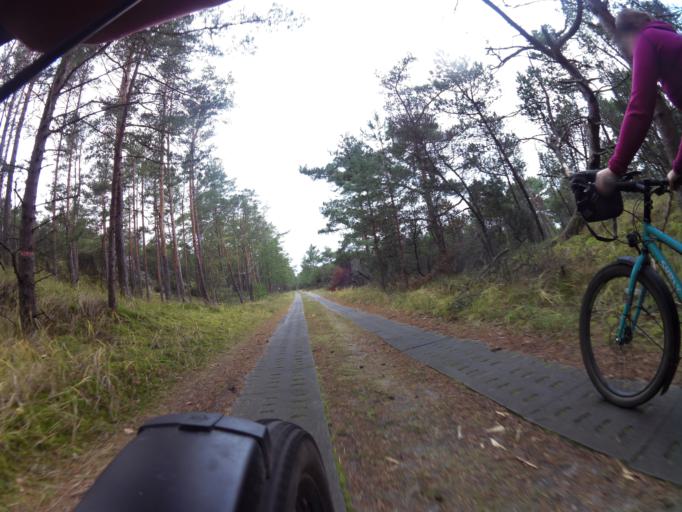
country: PL
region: Pomeranian Voivodeship
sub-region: Powiat pucki
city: Hel
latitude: 54.6269
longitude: 18.8146
